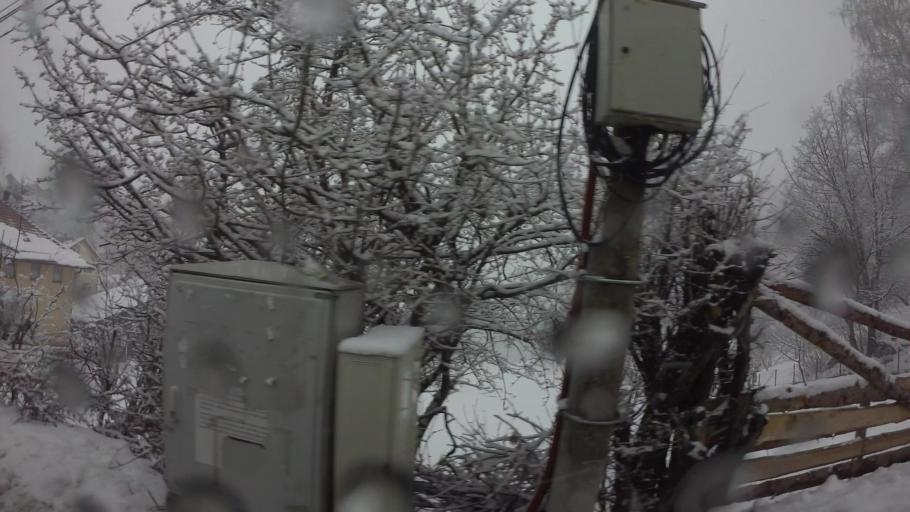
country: BA
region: Federation of Bosnia and Herzegovina
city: Kobilja Glava
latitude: 43.8508
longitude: 18.4515
